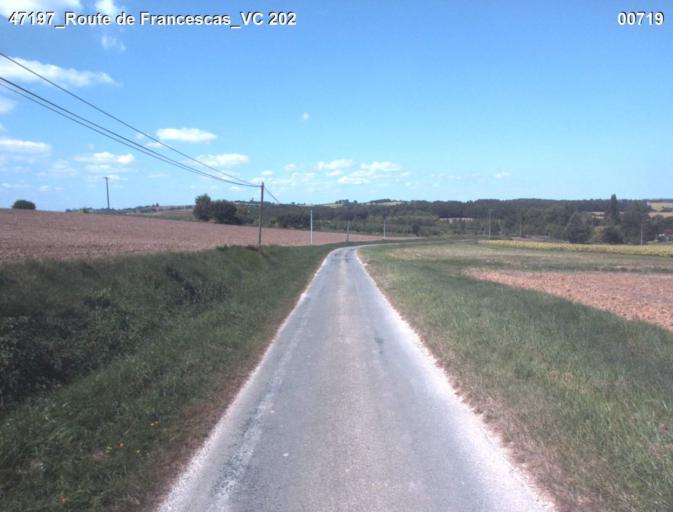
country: FR
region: Aquitaine
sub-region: Departement du Lot-et-Garonne
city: Laplume
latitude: 44.0685
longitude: 0.4670
